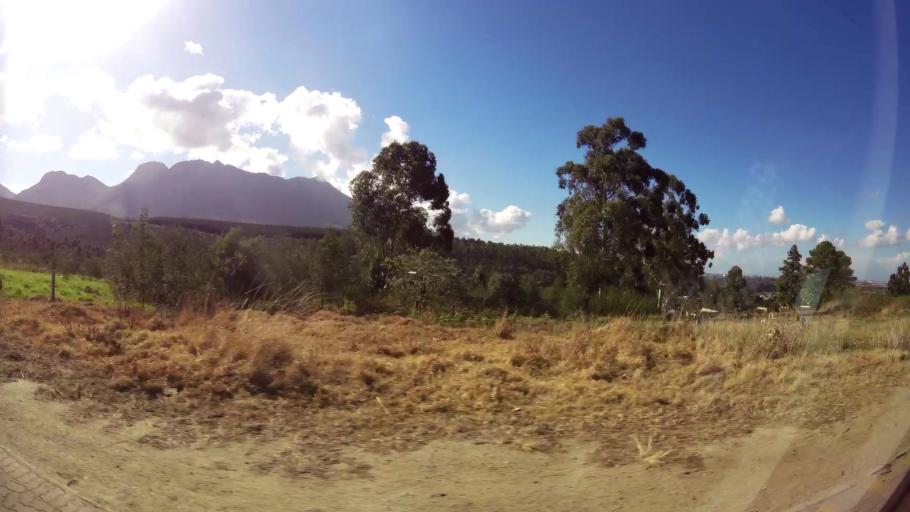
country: ZA
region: Western Cape
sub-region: Eden District Municipality
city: George
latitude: -33.9376
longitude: 22.4048
